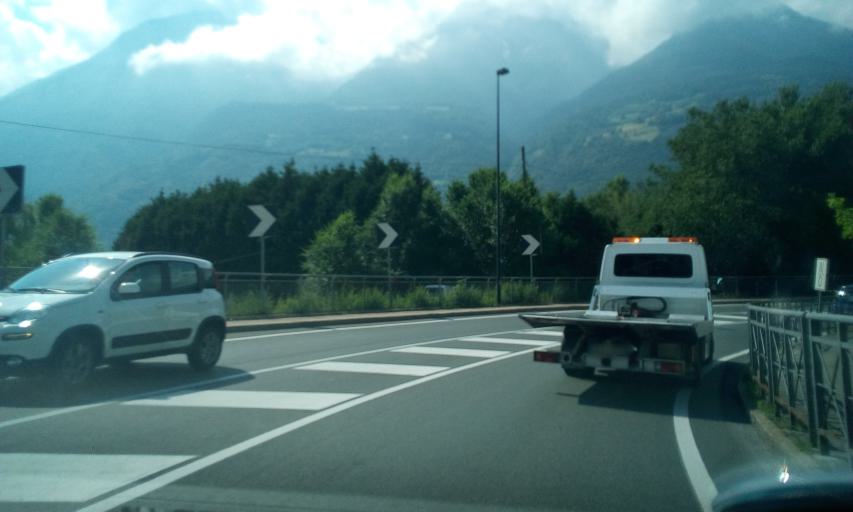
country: IT
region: Aosta Valley
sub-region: Valle d'Aosta
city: Pollein
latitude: 45.7365
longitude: 7.3404
